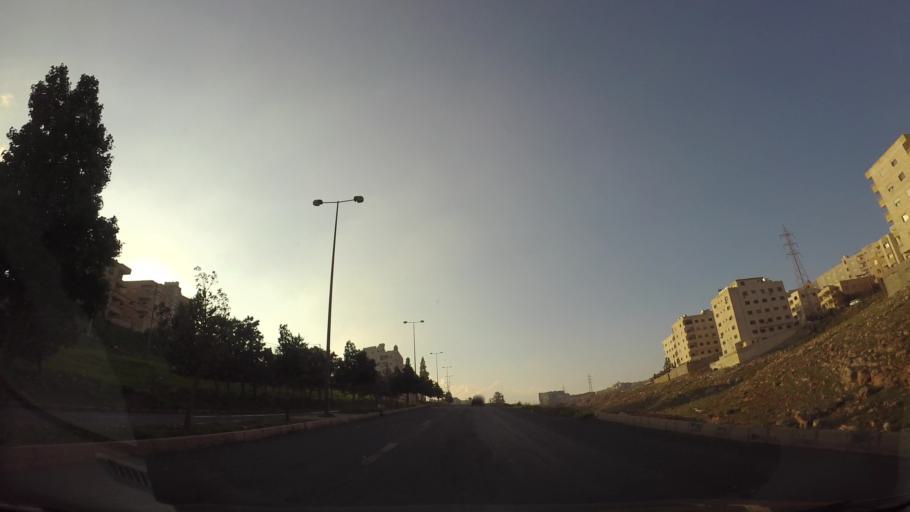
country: JO
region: Amman
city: Amman
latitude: 31.9841
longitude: 35.9564
